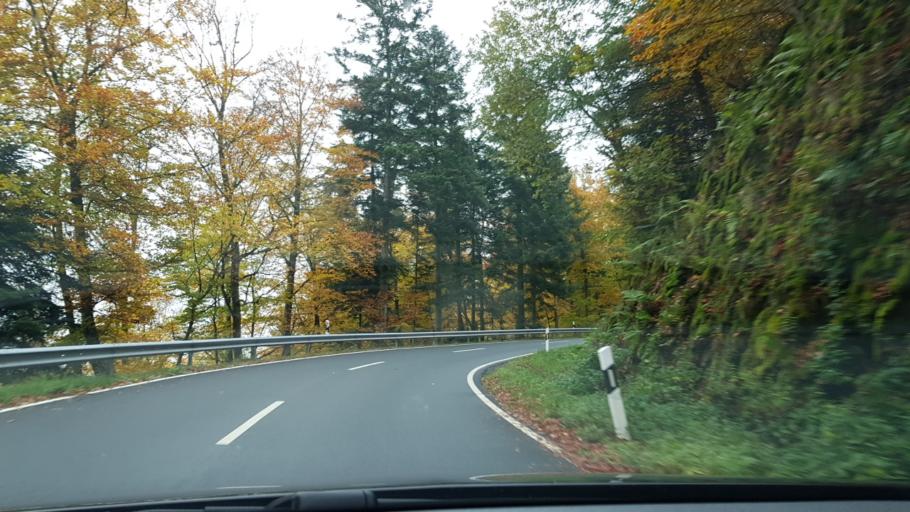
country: DE
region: Rheinland-Pfalz
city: Polich
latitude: 49.7832
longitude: 6.8501
